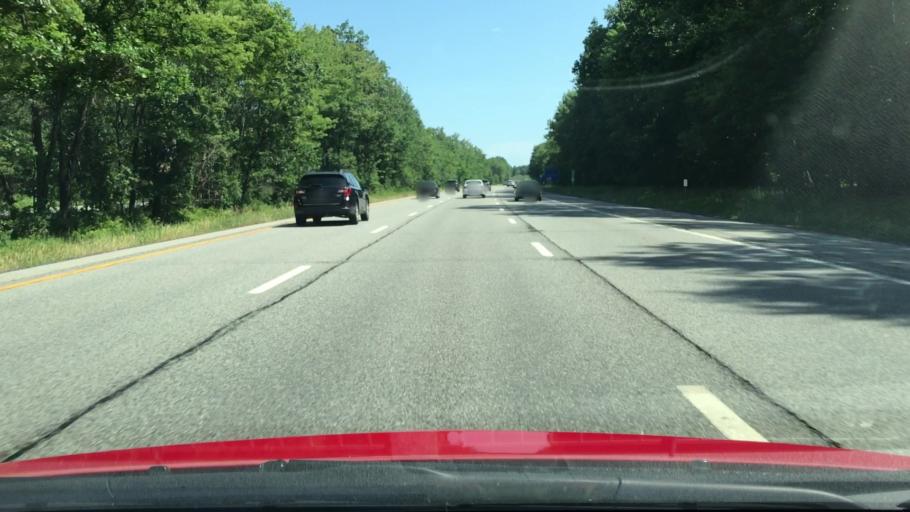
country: US
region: New York
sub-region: Saratoga County
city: Saratoga Springs
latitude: 43.1584
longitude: -73.7209
